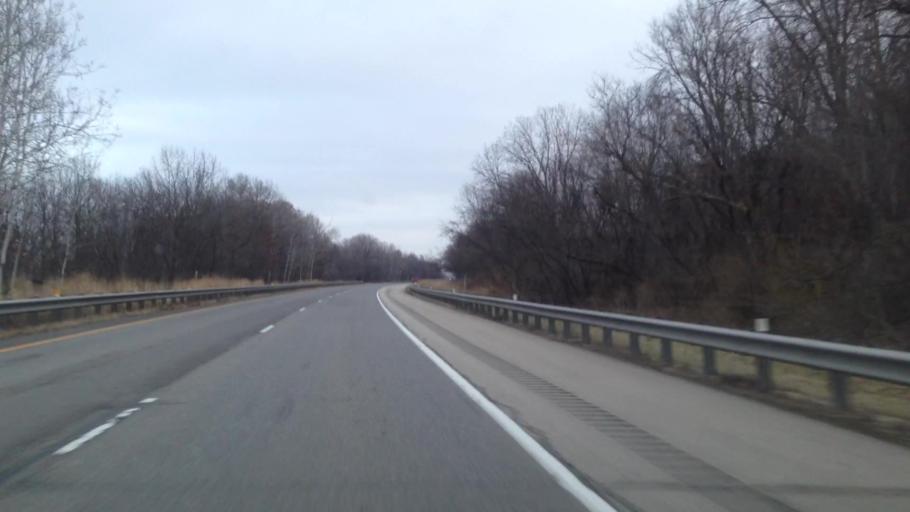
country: US
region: Wisconsin
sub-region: La Crosse County
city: Brice Prairie
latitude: 43.9196
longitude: -91.3804
